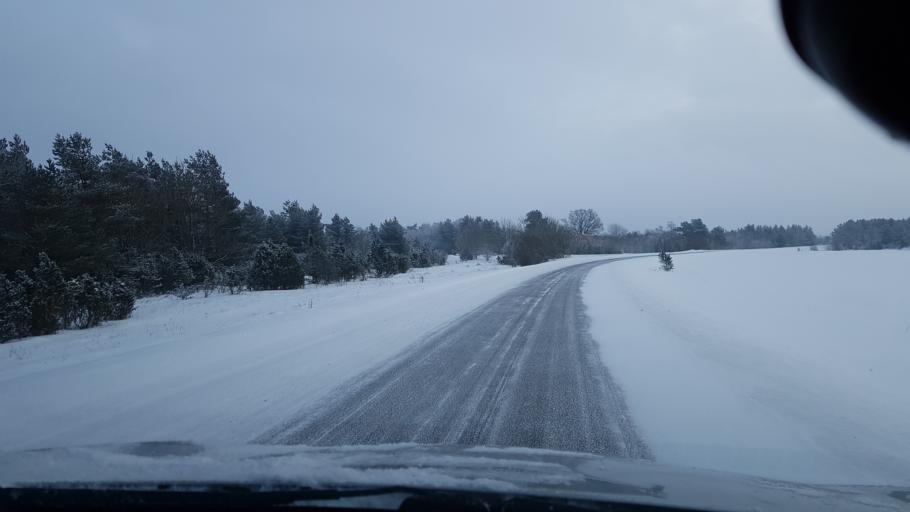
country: EE
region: Harju
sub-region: Keila linn
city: Keila
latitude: 59.3563
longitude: 24.4245
